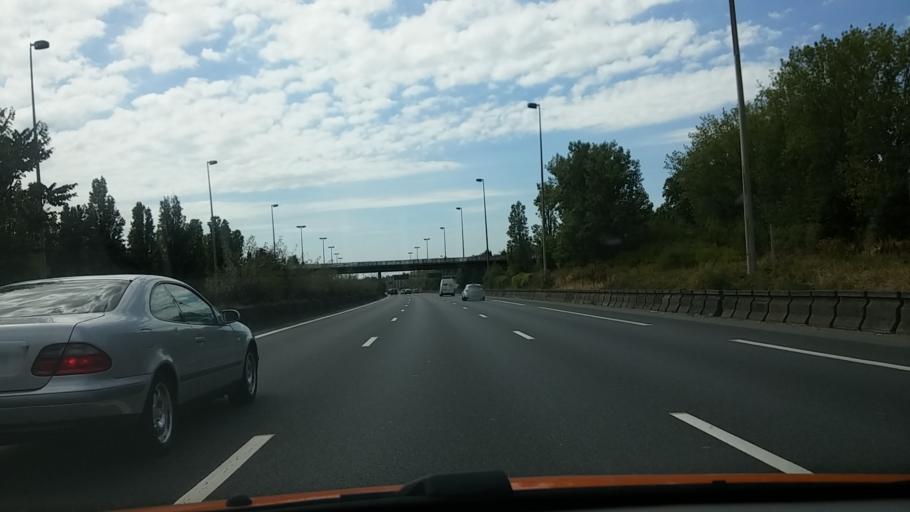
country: FR
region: Ile-de-France
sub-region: Departement du Val-de-Marne
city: Nogent-sur-Marne
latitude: 48.8302
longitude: 2.4890
